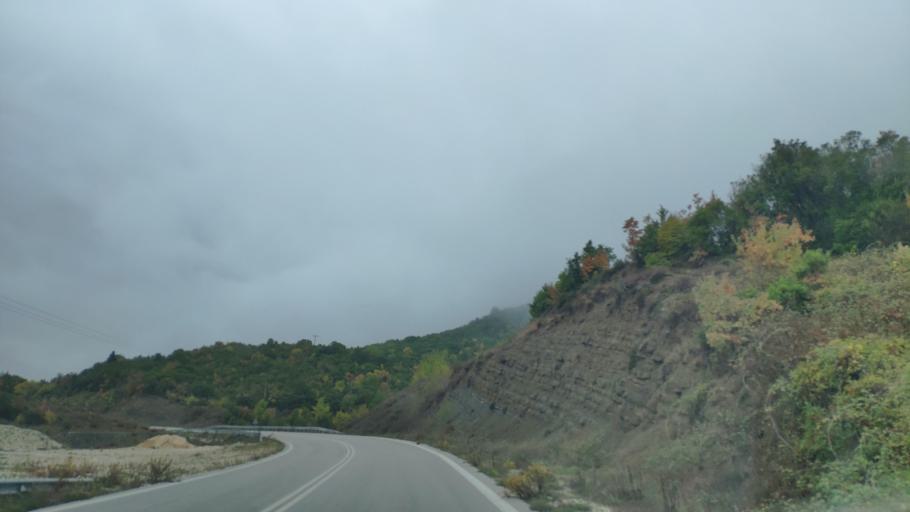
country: GR
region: Epirus
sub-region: Nomos Thesprotias
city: Paramythia
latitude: 39.4865
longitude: 20.6718
